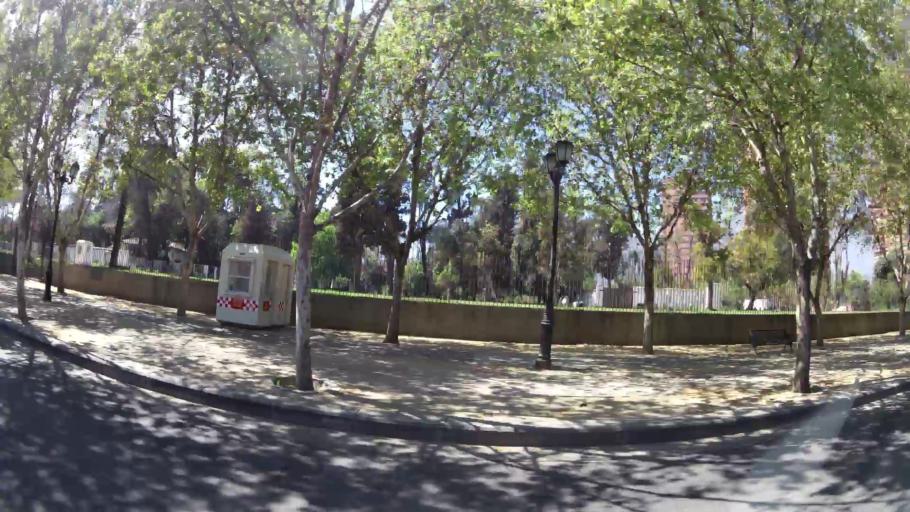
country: CL
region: Santiago Metropolitan
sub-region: Provincia de Santiago
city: Villa Presidente Frei, Nunoa, Santiago, Chile
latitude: -33.4193
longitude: -70.5404
